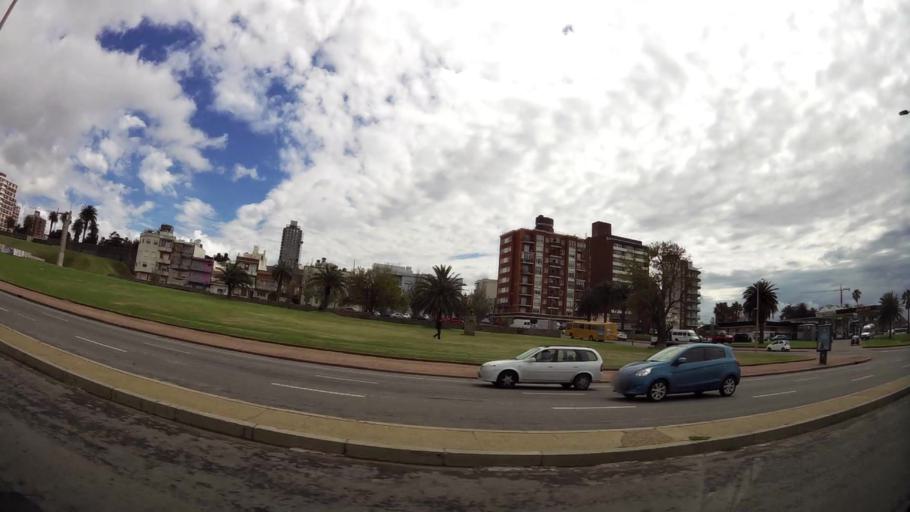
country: UY
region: Montevideo
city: Montevideo
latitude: -34.9155
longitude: -56.1861
